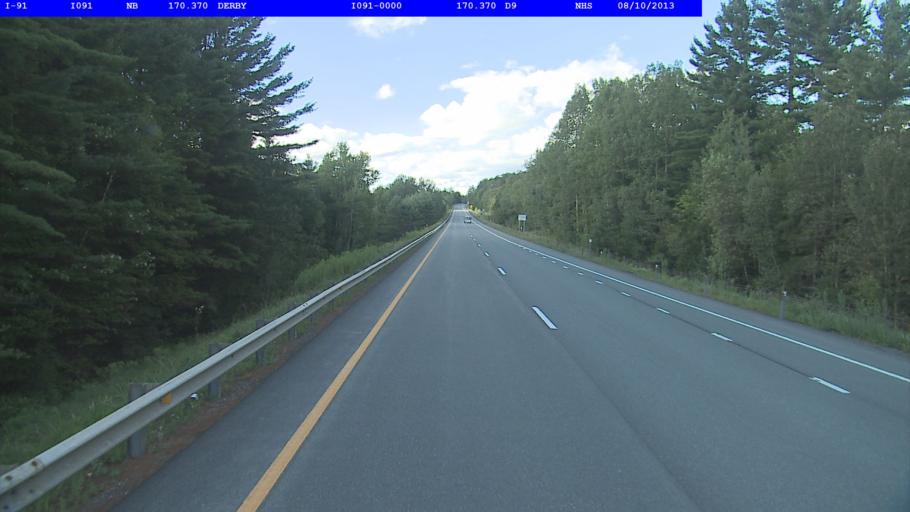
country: US
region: Vermont
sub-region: Orleans County
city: Newport
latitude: 44.9269
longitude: -72.1706
